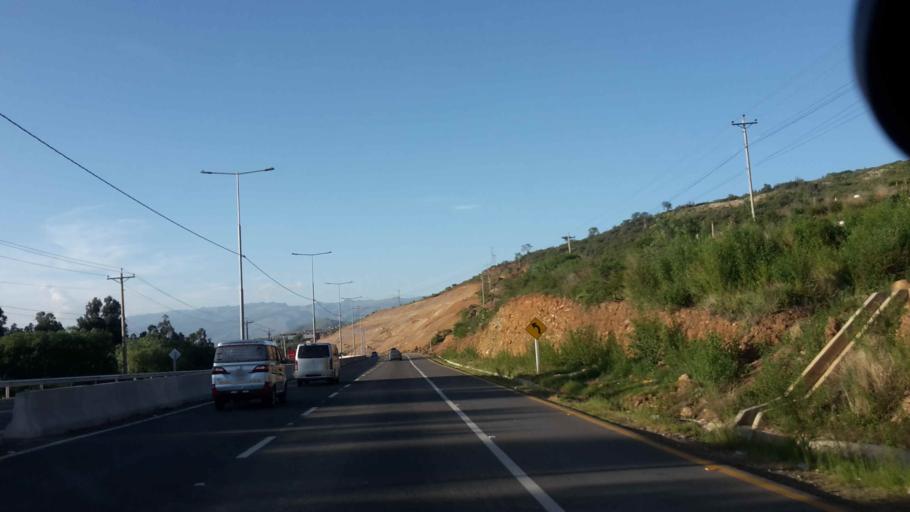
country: BO
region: Cochabamba
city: Tarata
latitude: -17.5205
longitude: -66.0863
